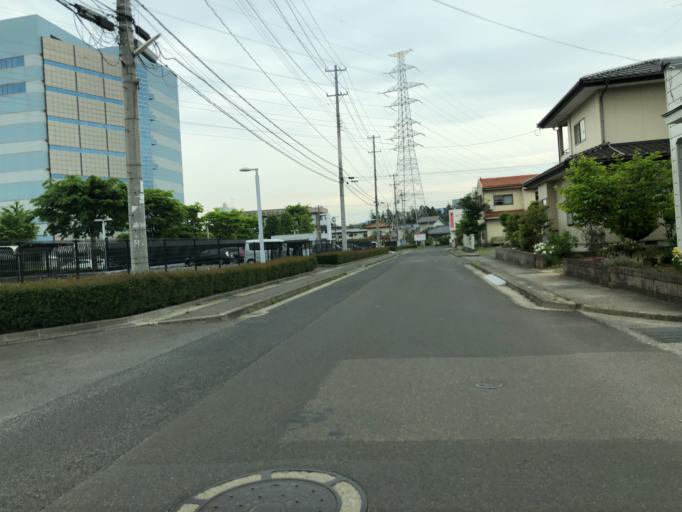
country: JP
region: Fukushima
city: Fukushima-shi
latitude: 37.8041
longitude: 140.4480
